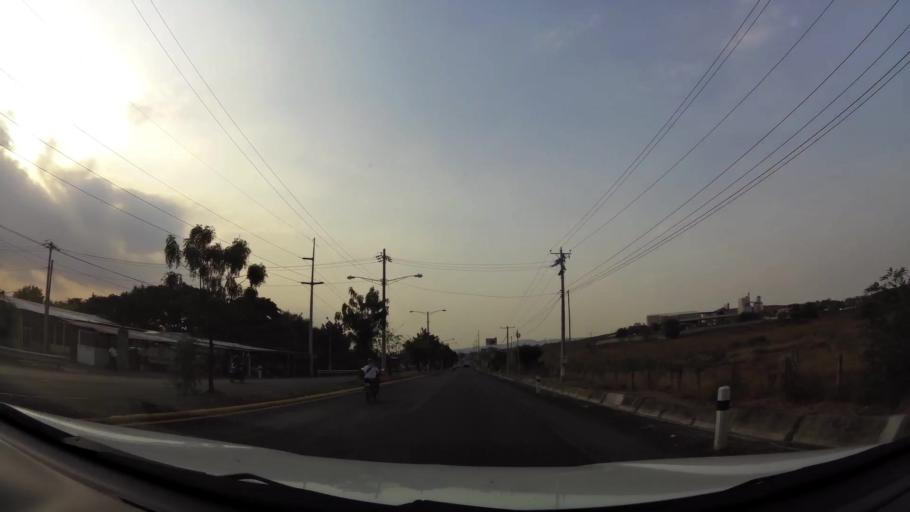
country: NI
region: Managua
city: Ciudad Sandino
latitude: 12.1519
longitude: -86.3369
